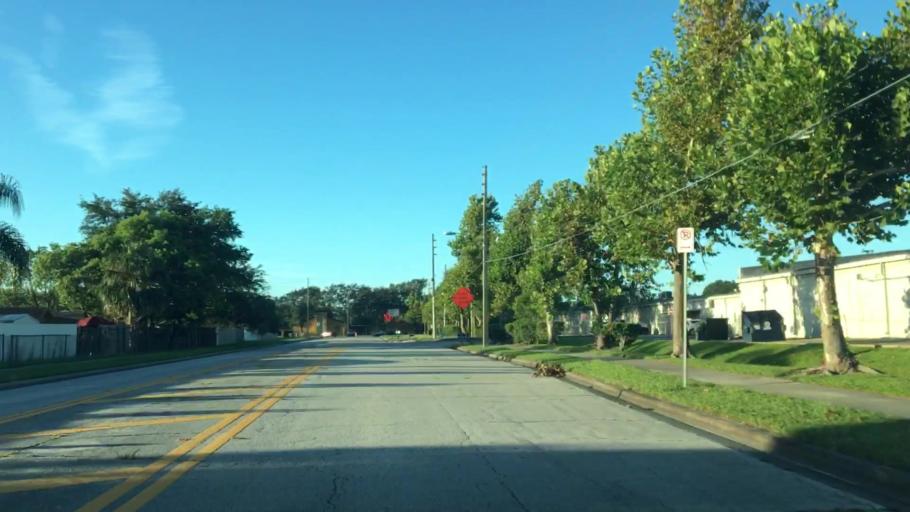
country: US
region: Florida
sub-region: Orange County
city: Conway
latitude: 28.4825
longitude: -81.3068
